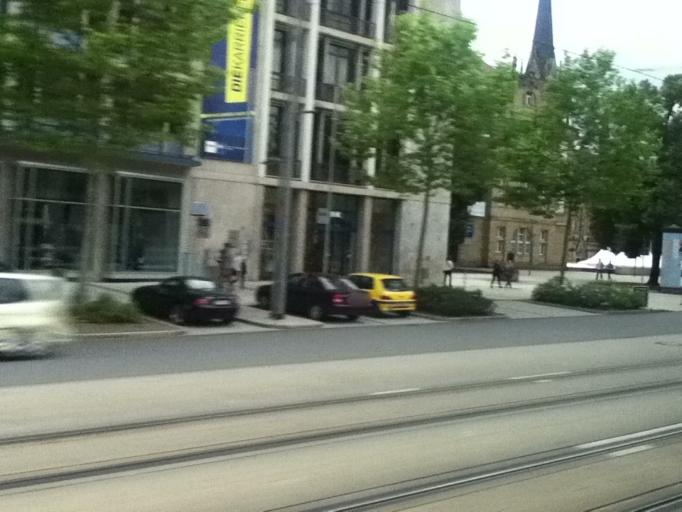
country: DE
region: Saxony
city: Chemnitz
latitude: 50.8367
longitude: 12.9254
